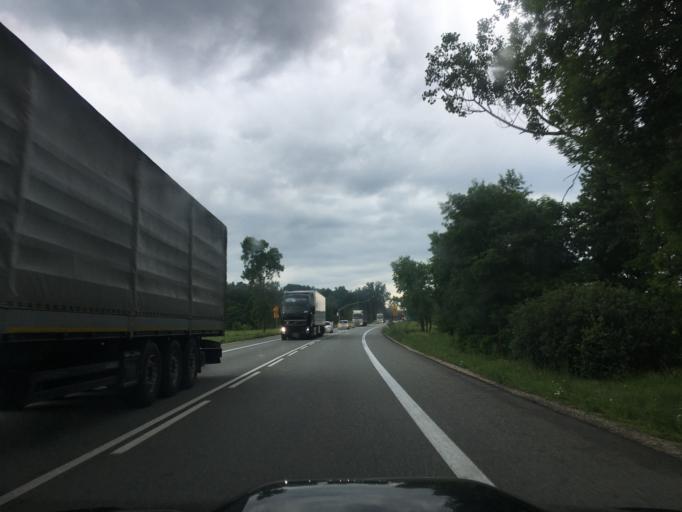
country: PL
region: Masovian Voivodeship
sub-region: Powiat otwocki
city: Celestynow
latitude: 52.0409
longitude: 21.3939
